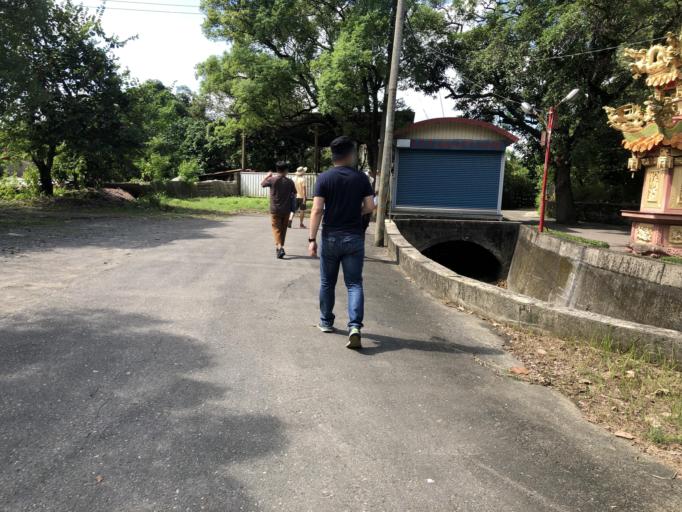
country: TW
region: Taiwan
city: Yujing
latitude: 22.9049
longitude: 120.5231
